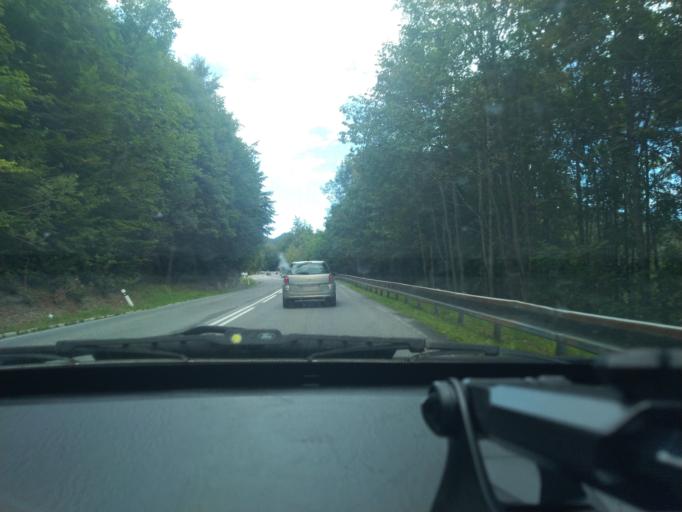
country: SK
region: Banskobystricky
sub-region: Okres Ziar nad Hronom
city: Kremnica
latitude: 48.8316
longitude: 19.0120
